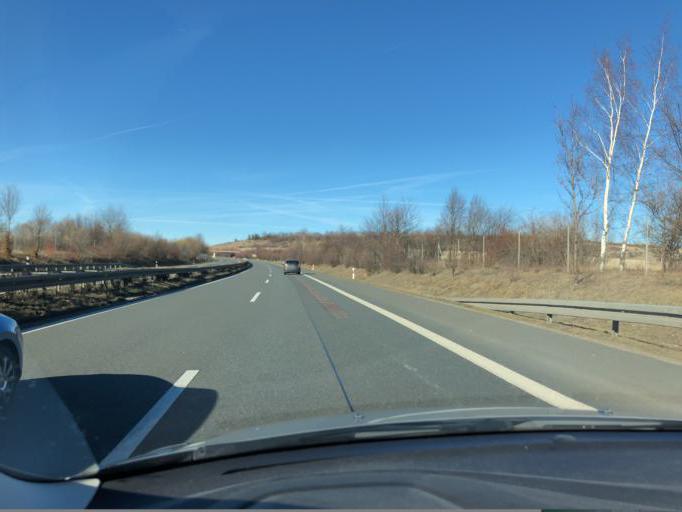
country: DE
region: Saxony-Anhalt
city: Veckenstedt
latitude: 51.8940
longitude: 10.7075
